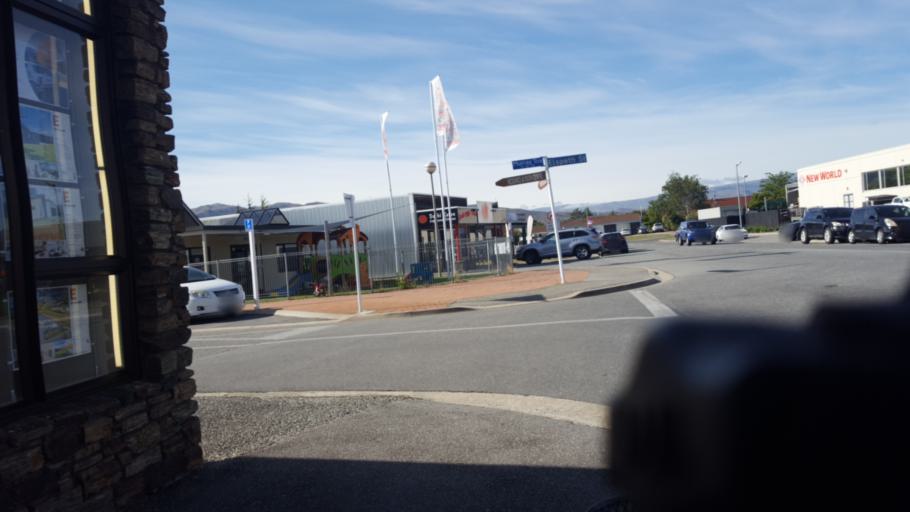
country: NZ
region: Otago
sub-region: Queenstown-Lakes District
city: Wanaka
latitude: -45.0370
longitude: 169.1950
